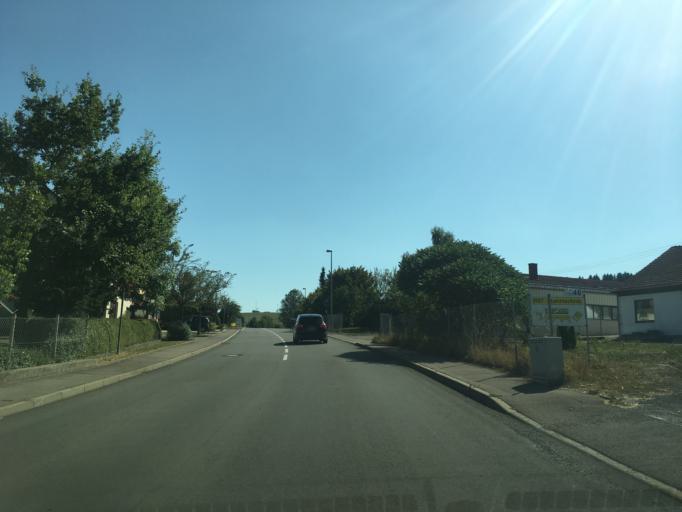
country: DE
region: Baden-Wuerttemberg
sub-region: Tuebingen Region
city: Munsingen
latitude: 48.4064
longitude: 9.4883
